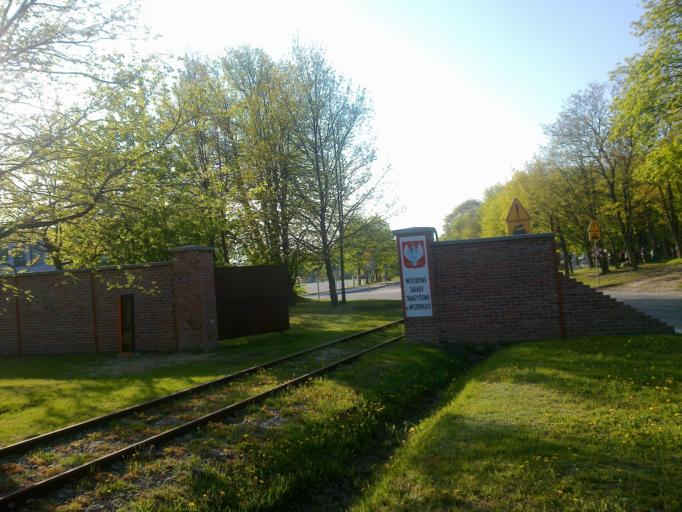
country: PL
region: Pomeranian Voivodeship
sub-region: Gdansk
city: Gdansk
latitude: 54.4034
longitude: 18.6826
